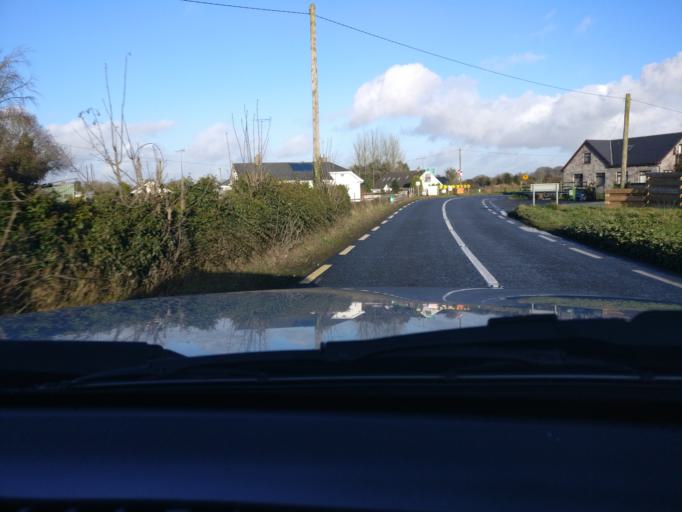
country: IE
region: Leinster
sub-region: An Iarmhi
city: Rathwire
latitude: 53.5698
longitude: -7.1890
